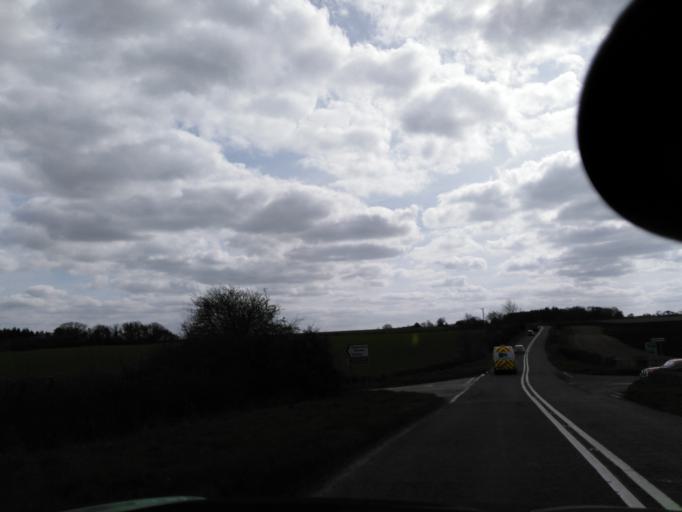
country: GB
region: England
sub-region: Wiltshire
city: Hankerton
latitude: 51.6555
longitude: -2.0534
